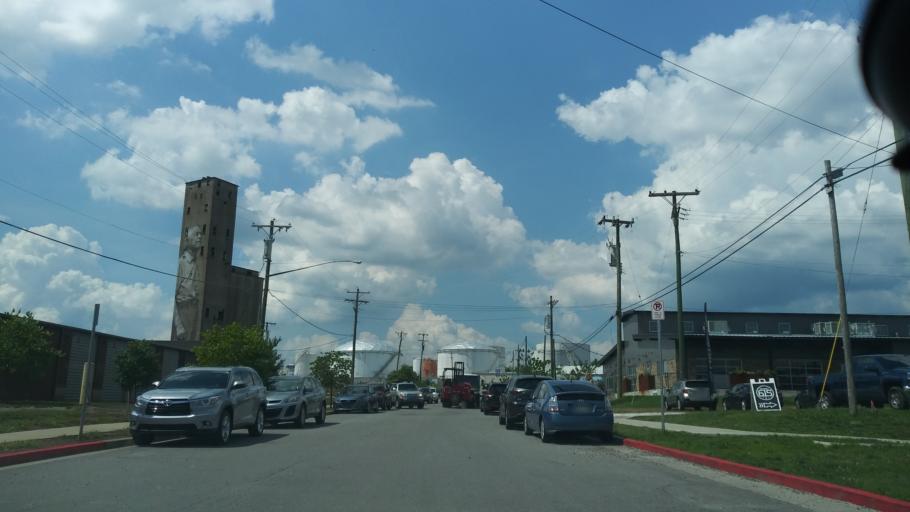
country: US
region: Tennessee
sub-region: Davidson County
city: Nashville
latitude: 36.1625
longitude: -86.8491
